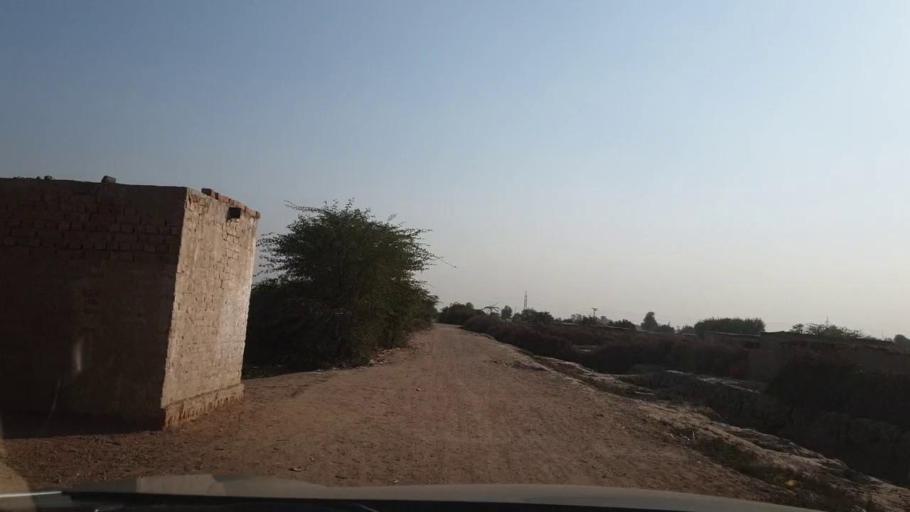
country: PK
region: Sindh
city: Tando Allahyar
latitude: 25.5056
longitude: 68.8400
